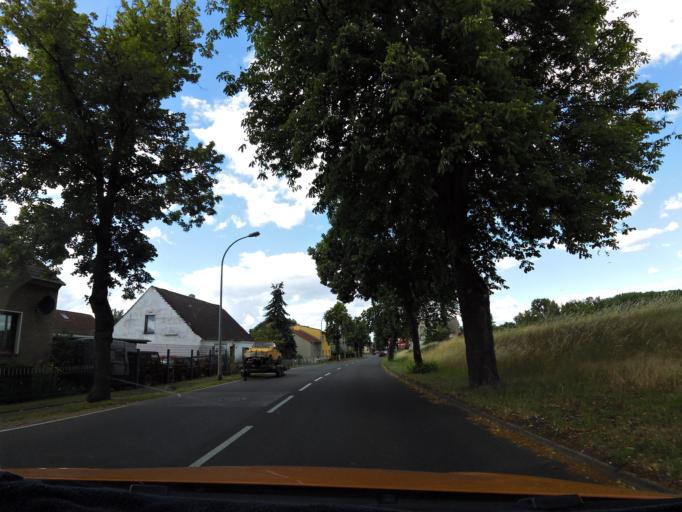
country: DE
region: Brandenburg
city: Rangsdorf
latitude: 52.3418
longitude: 13.4347
